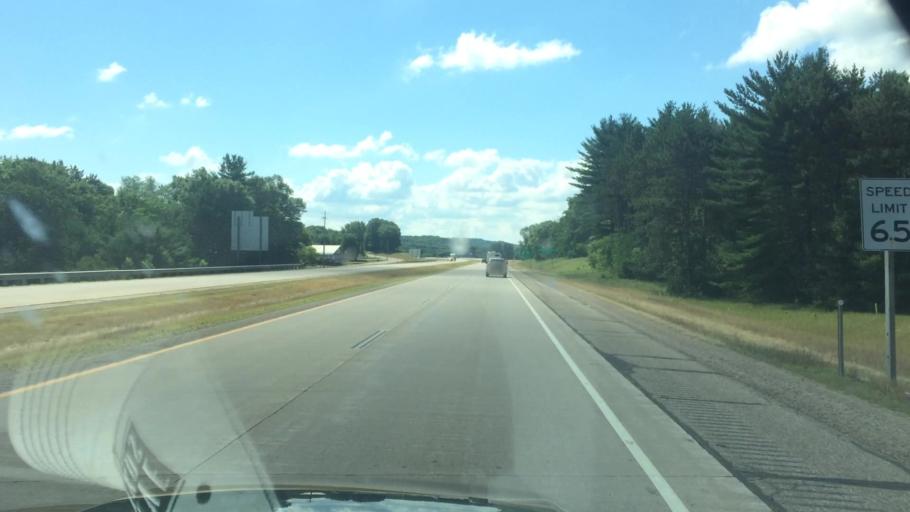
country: US
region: Wisconsin
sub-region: Waupaca County
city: Waupaca
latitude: 44.3484
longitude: -89.1052
